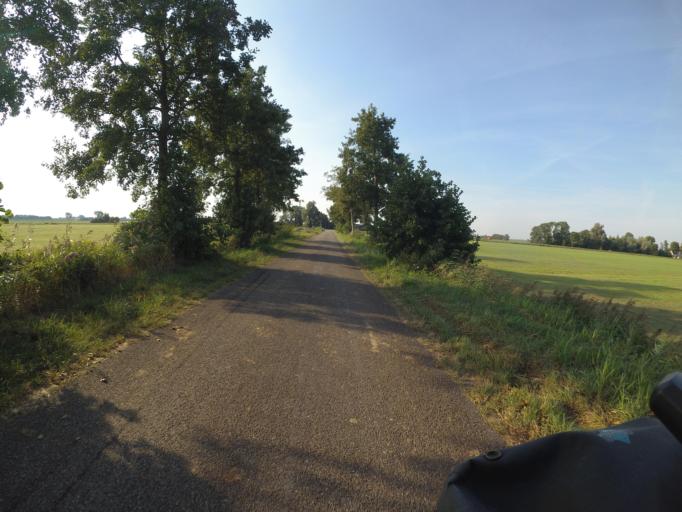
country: NL
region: Overijssel
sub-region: Gemeente Steenwijkerland
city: Oldemarkt
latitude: 52.8191
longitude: 5.8934
